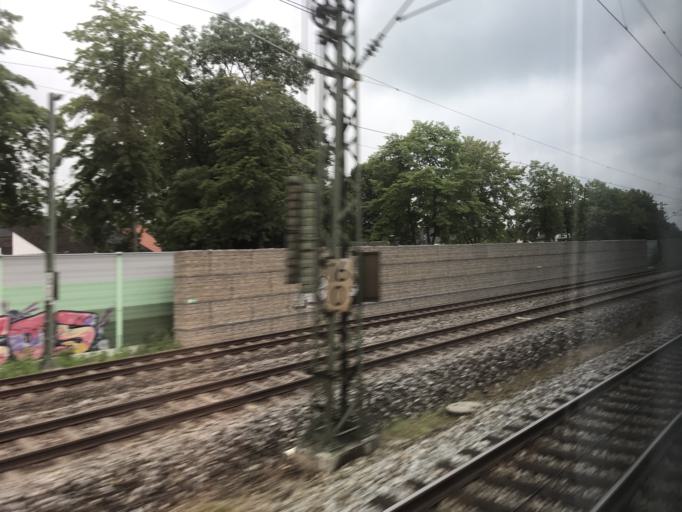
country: DE
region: Bavaria
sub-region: Upper Bavaria
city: Grobenzell
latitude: 48.1969
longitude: 11.3707
